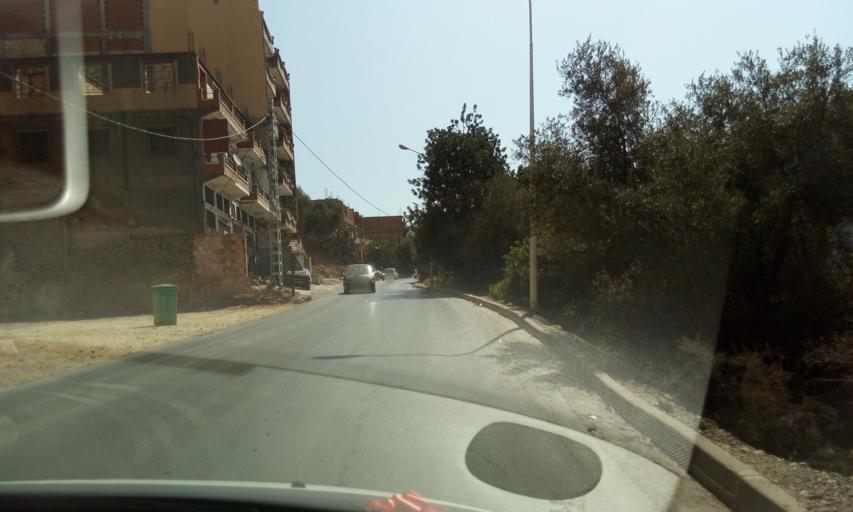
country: DZ
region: Bejaia
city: Seddouk
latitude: 36.6151
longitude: 4.6957
